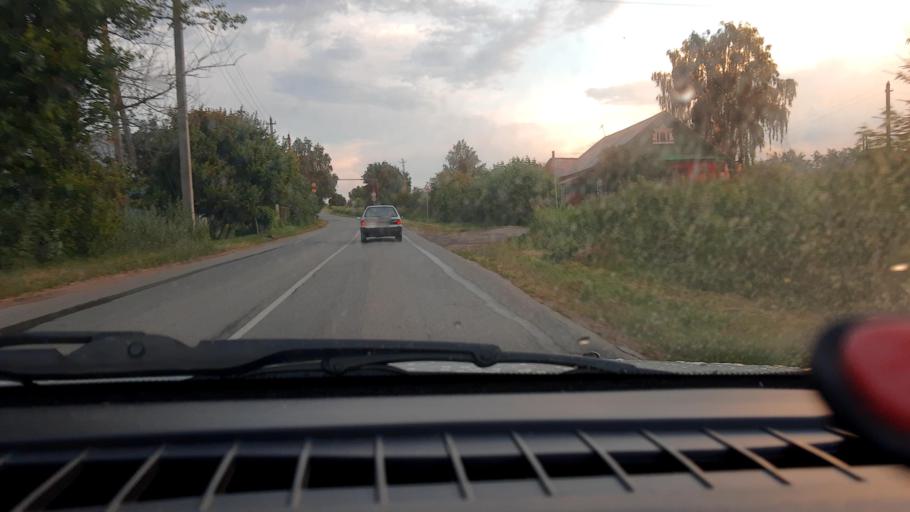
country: RU
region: Nizjnij Novgorod
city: Afonino
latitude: 56.1304
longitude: 44.0294
